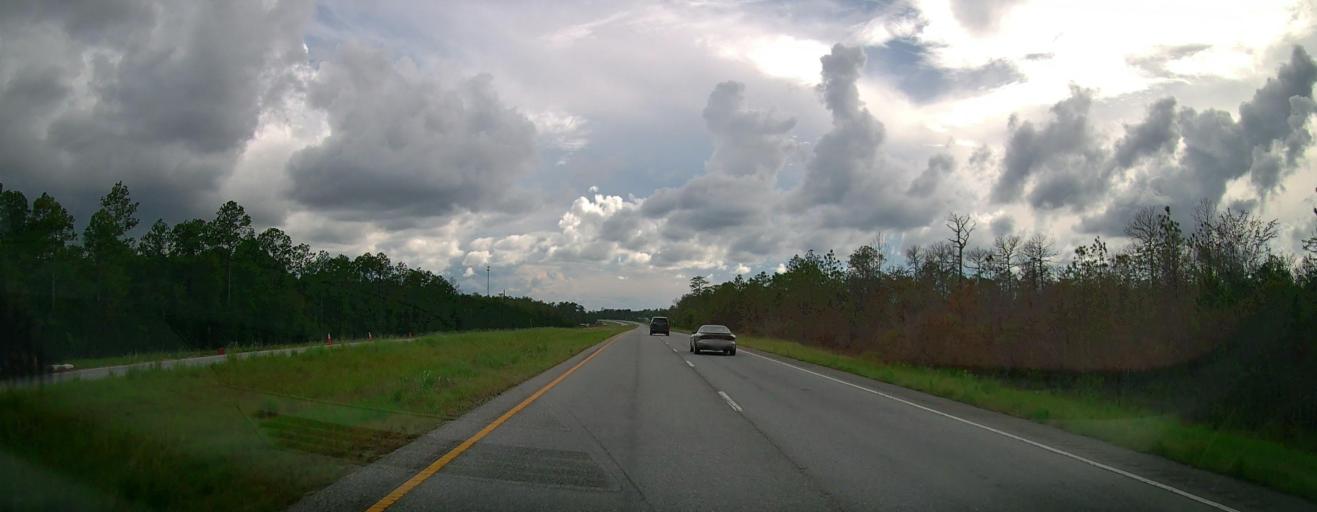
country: US
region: Georgia
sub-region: Pierce County
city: Blackshear
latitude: 31.4398
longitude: -82.0794
